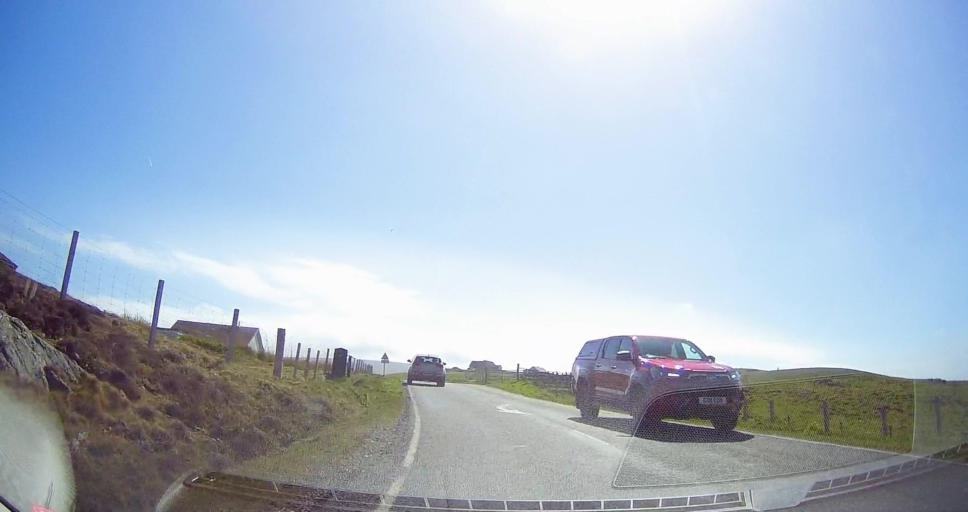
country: GB
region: Scotland
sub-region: Shetland Islands
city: Sandwick
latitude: 60.1032
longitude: -1.3256
